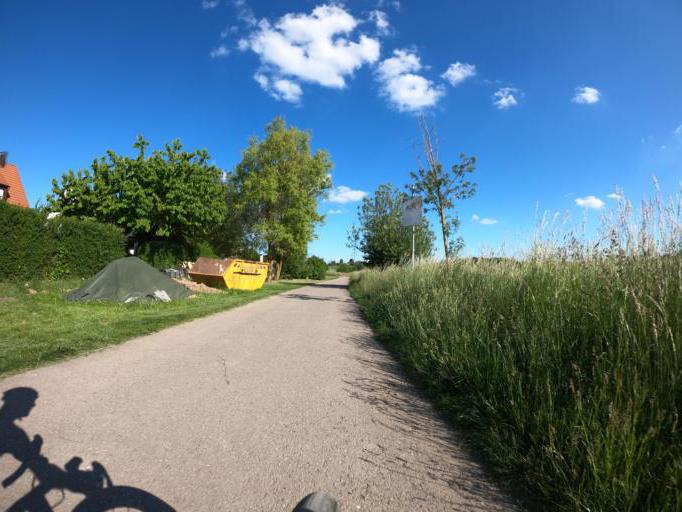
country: DE
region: Baden-Wuerttemberg
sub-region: Regierungsbezirk Stuttgart
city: Magstadt
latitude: 48.7365
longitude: 8.9766
